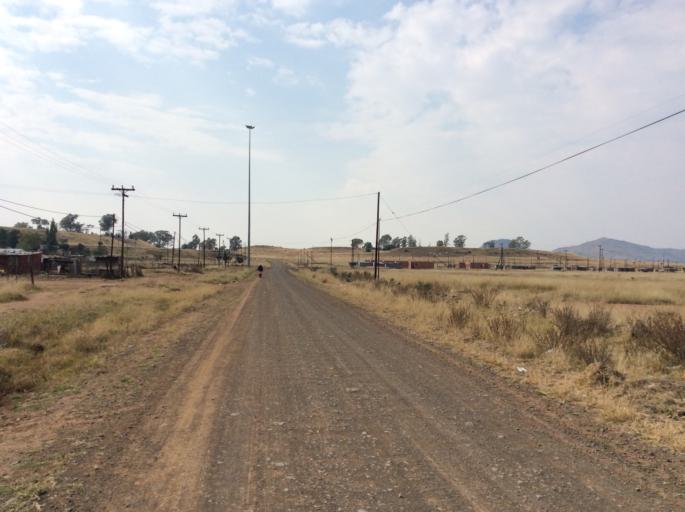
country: LS
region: Mafeteng
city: Mafeteng
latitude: -29.9900
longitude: 27.0019
